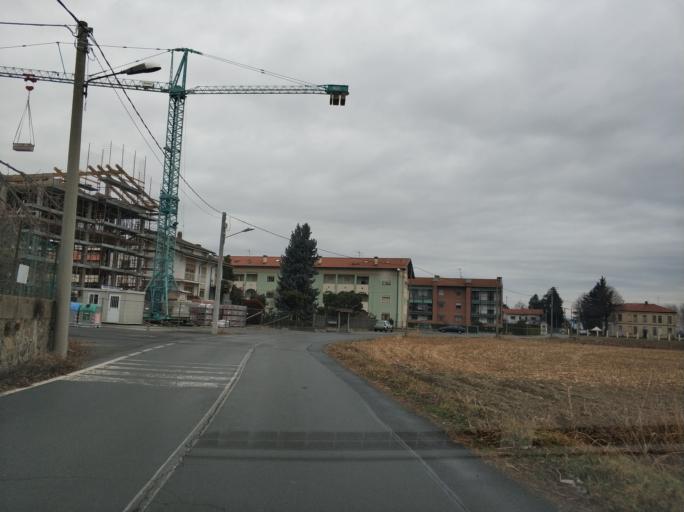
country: IT
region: Piedmont
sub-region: Provincia di Torino
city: Pavone Canavese
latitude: 45.4412
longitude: 7.8752
